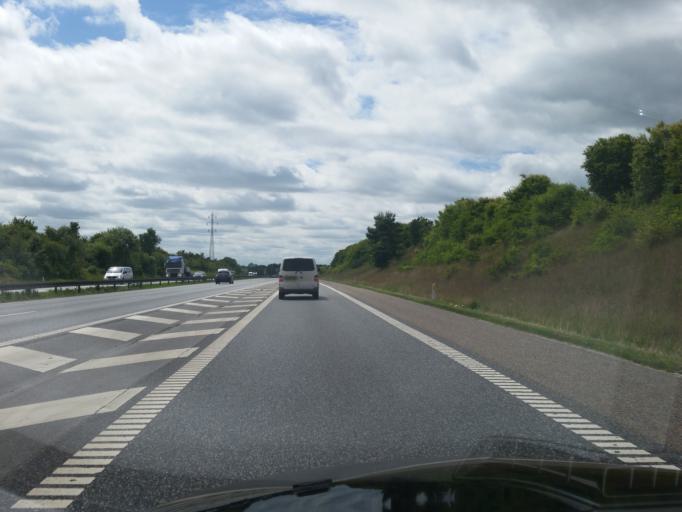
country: DK
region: Central Jutland
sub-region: Horsens Kommune
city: Horsens
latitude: 55.8831
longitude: 9.7870
